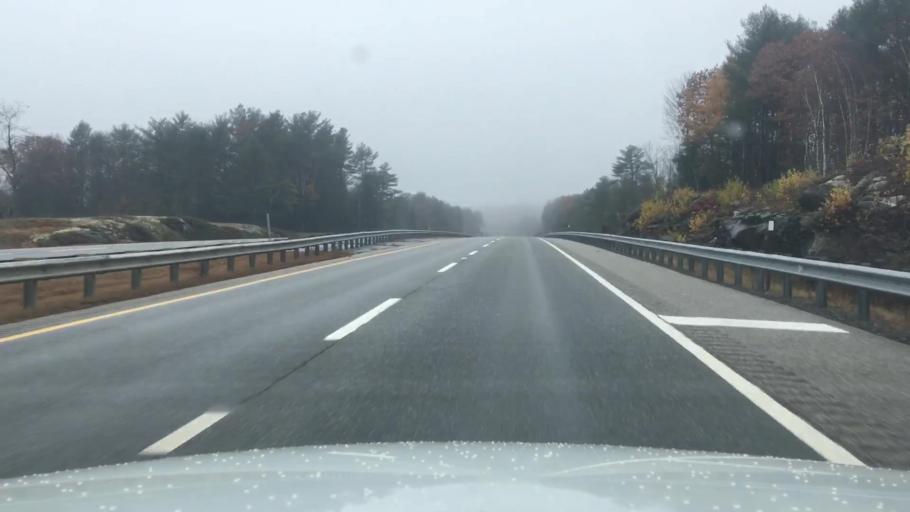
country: US
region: Maine
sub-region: Androscoggin County
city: Sabattus
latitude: 44.1246
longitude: -70.0218
